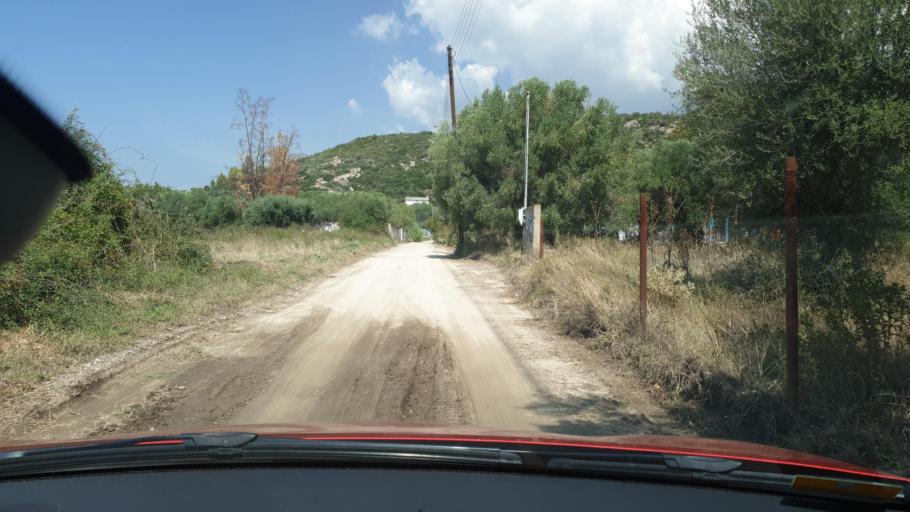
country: GR
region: Central Macedonia
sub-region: Nomos Chalkidikis
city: Sykia
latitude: 39.9848
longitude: 23.9083
